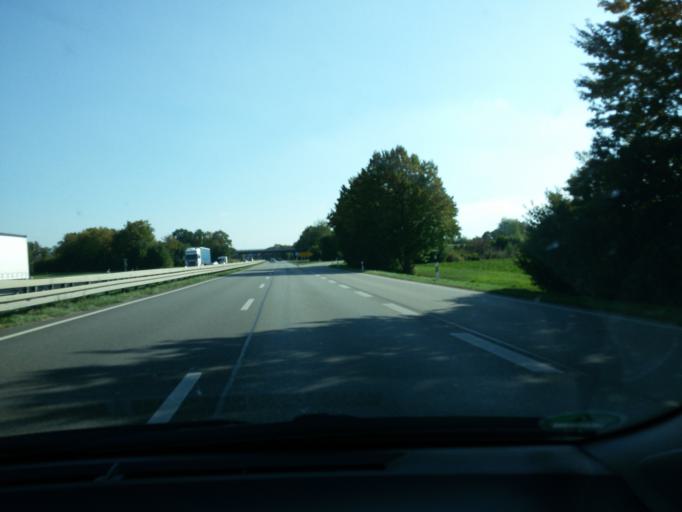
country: DE
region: Bavaria
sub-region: Swabia
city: Asbach-Baumenheim
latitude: 48.7054
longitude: 10.8052
